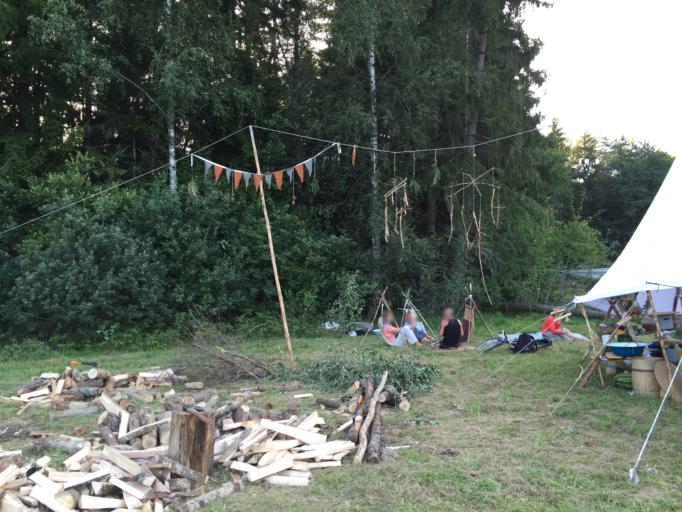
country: LT
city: Zarasai
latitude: 55.7904
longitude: 25.9626
